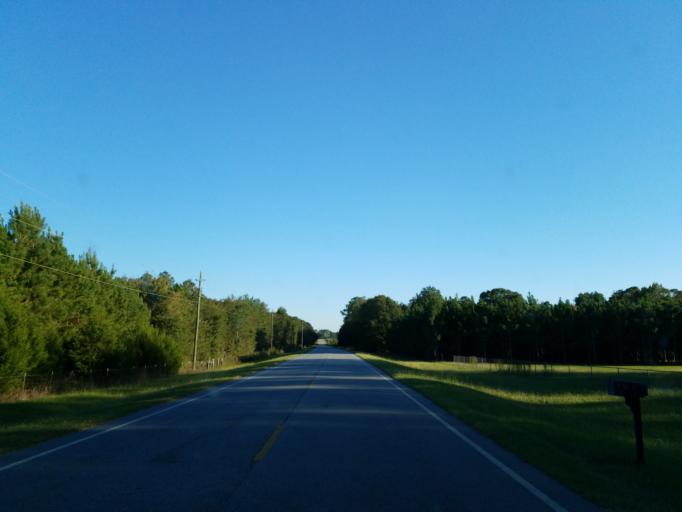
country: US
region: Georgia
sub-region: Worth County
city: Sylvester
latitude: 31.6920
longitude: -83.8838
